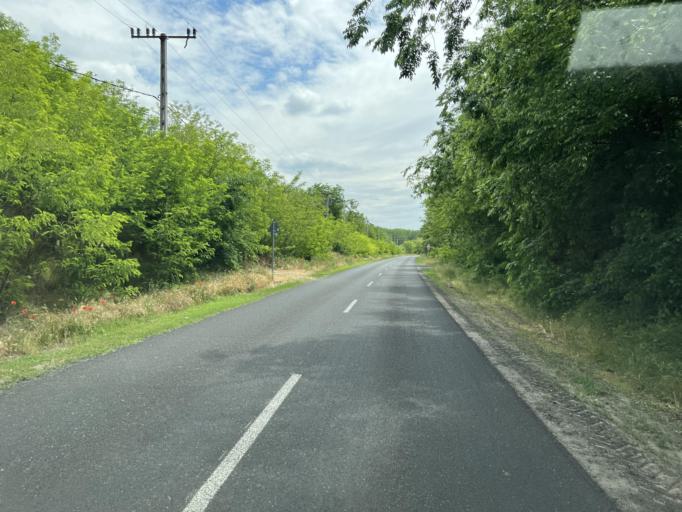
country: HU
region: Pest
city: Tapioszecso
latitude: 47.4769
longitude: 19.6114
